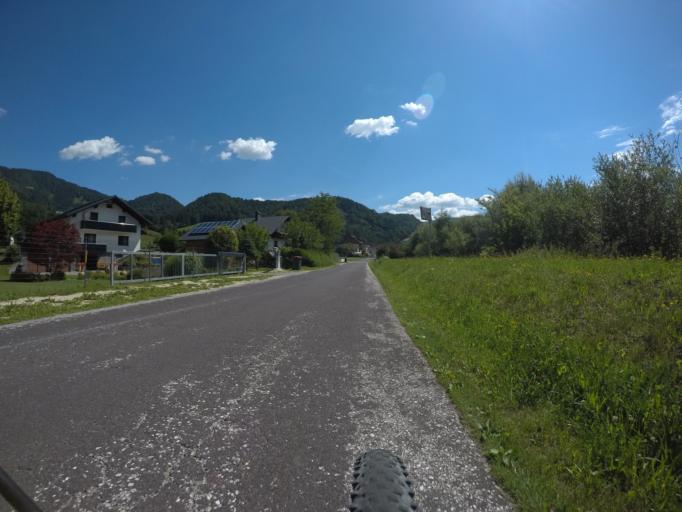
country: AT
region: Lower Austria
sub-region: Politischer Bezirk Scheibbs
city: Gostling an der Ybbs
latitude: 47.8417
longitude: 14.9109
